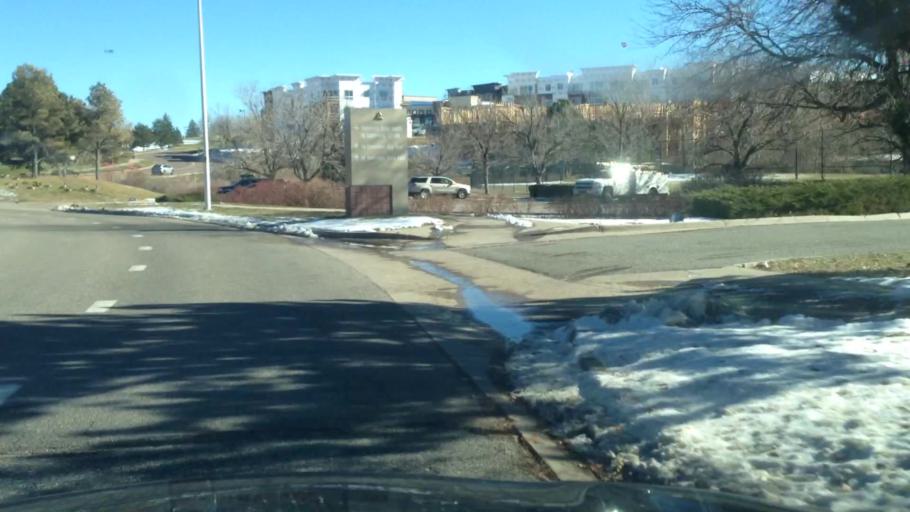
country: US
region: Colorado
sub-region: Douglas County
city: Meridian
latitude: 39.5646
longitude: -104.8620
